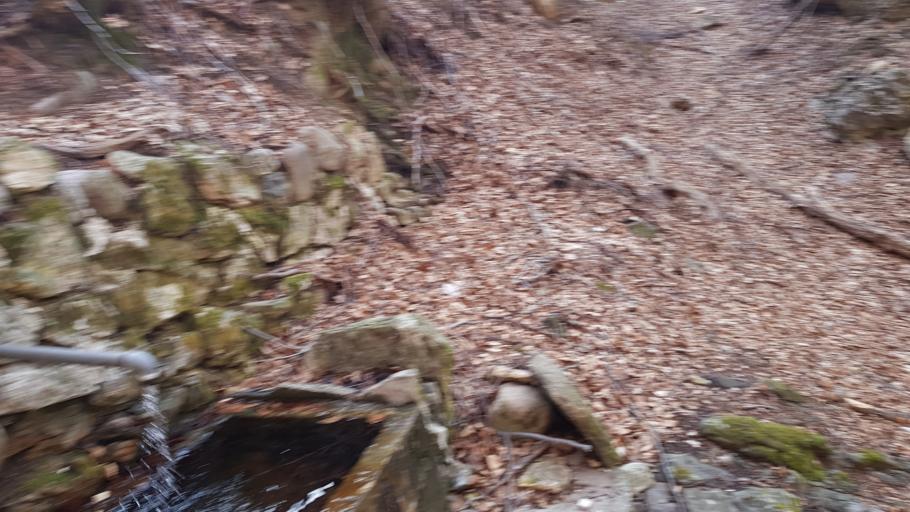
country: IT
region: Trentino-Alto Adige
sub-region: Provincia di Trento
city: Vezzano
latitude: 46.0647
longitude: 11.0191
